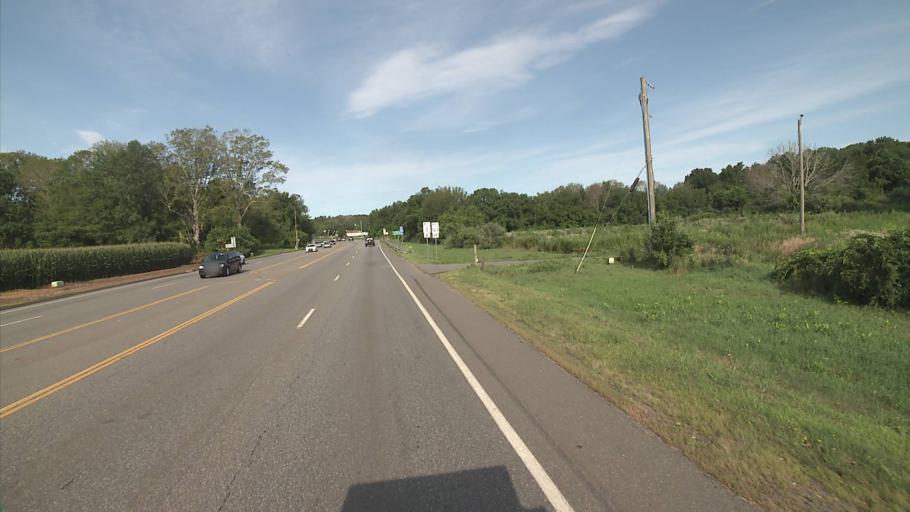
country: US
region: Connecticut
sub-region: New London County
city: Preston City
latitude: 41.4883
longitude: -71.9812
